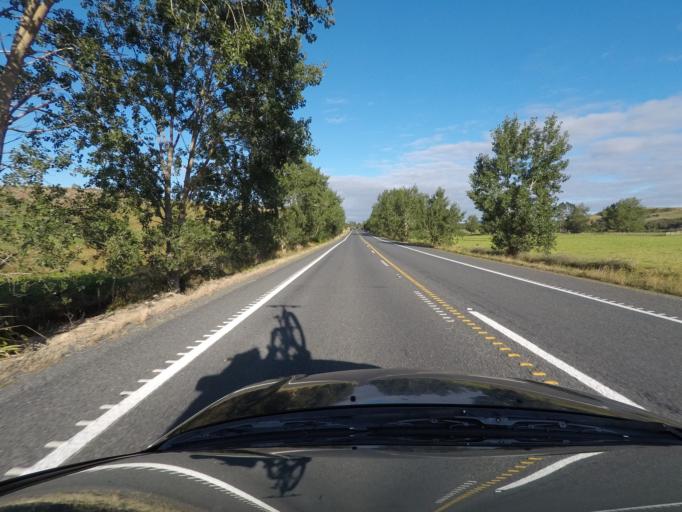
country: NZ
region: Northland
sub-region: Far North District
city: Kawakawa
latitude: -35.5190
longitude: 174.1951
